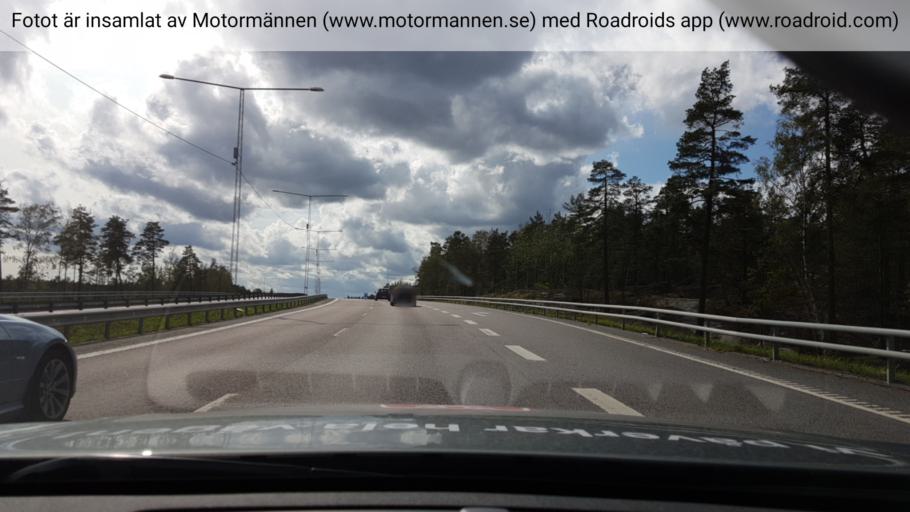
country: SE
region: Stockholm
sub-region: Nacka Kommun
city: Alta
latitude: 59.2499
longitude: 18.2004
